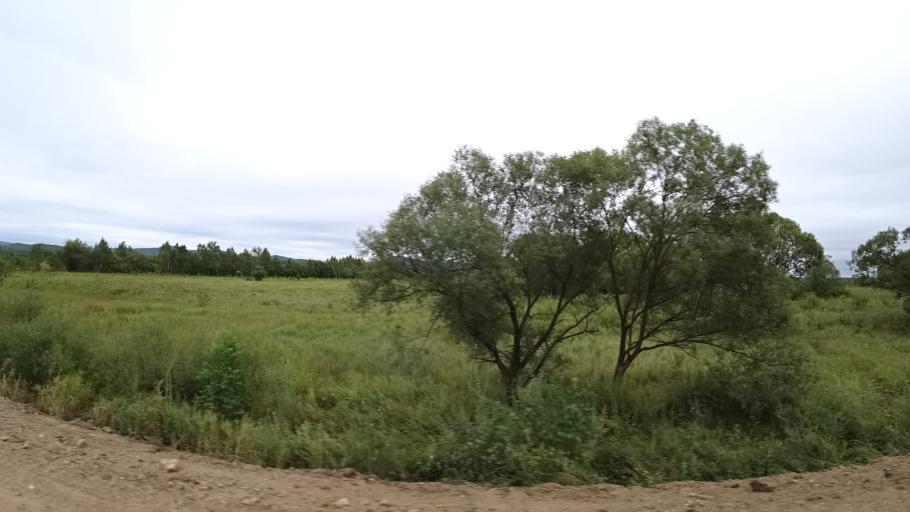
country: RU
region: Primorskiy
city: Rettikhovka
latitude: 44.1436
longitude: 132.6692
